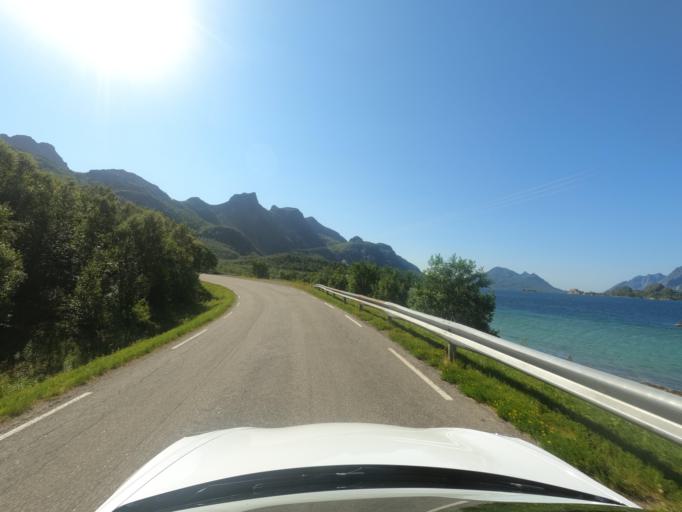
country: NO
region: Nordland
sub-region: Hadsel
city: Stokmarknes
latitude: 68.3579
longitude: 15.0633
